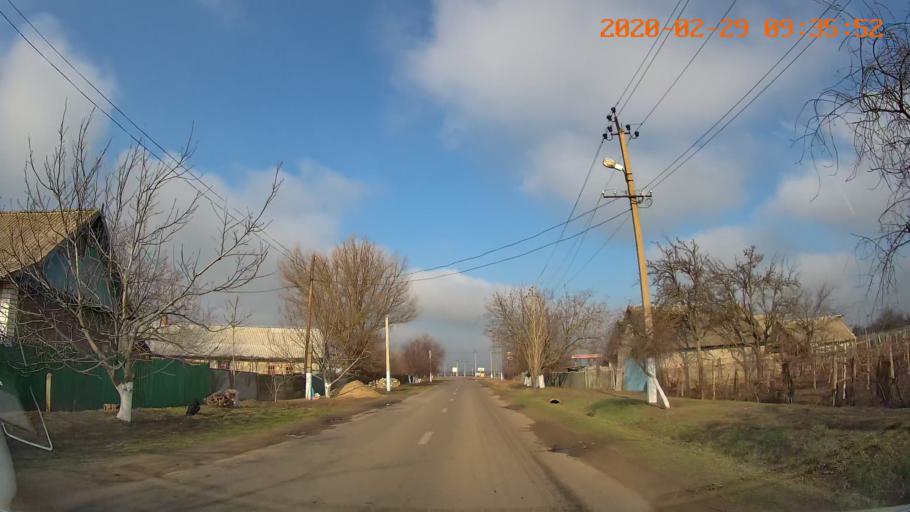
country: MD
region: Telenesti
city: Dnestrovsc
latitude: 46.6214
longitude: 29.8950
